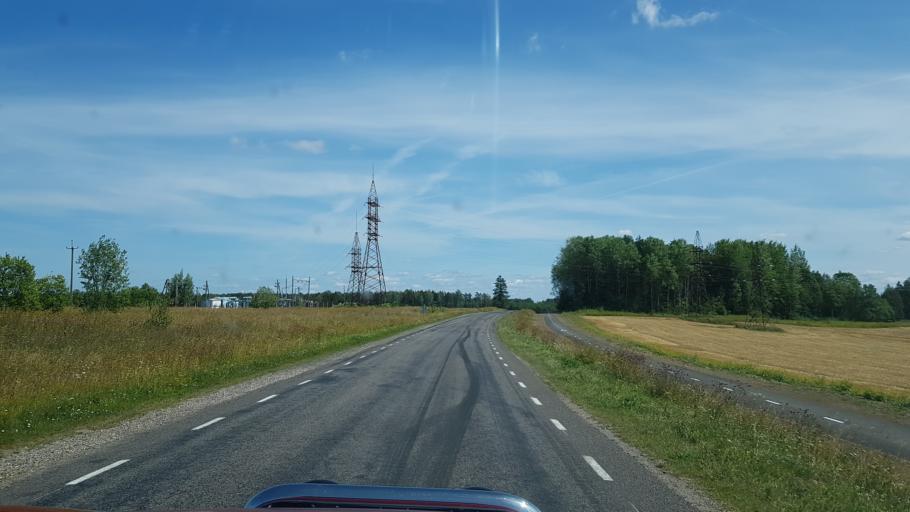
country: EE
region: Jaervamaa
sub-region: Jaerva-Jaani vald
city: Jarva-Jaani
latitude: 59.0389
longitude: 25.8948
